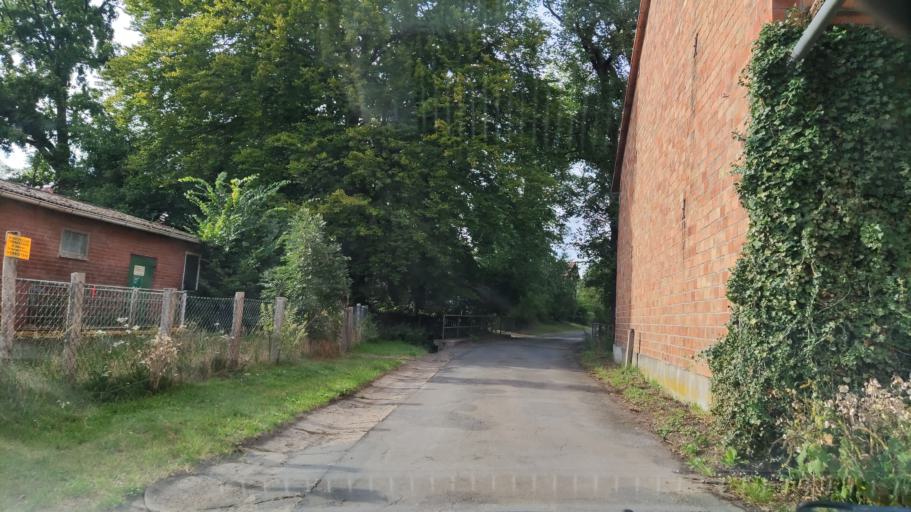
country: DE
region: Lower Saxony
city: Jameln
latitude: 53.0415
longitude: 11.0765
